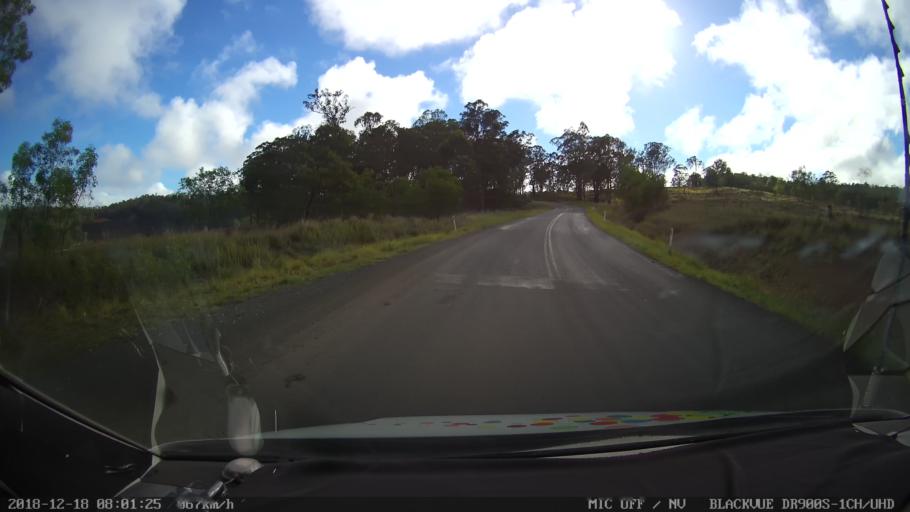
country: AU
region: New South Wales
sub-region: Kyogle
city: Kyogle
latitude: -28.3899
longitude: 152.6230
